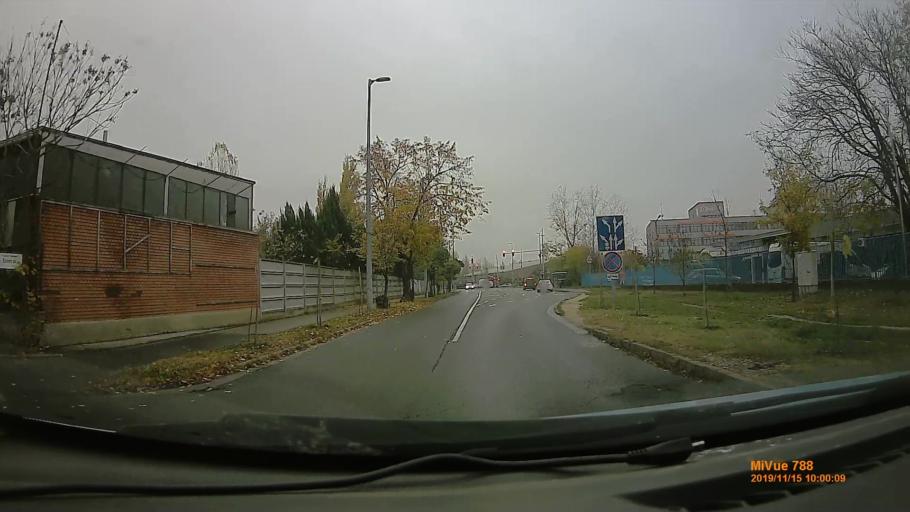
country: HU
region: Budapest
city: Budapest XX. keruelet
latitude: 47.4642
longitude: 19.1028
